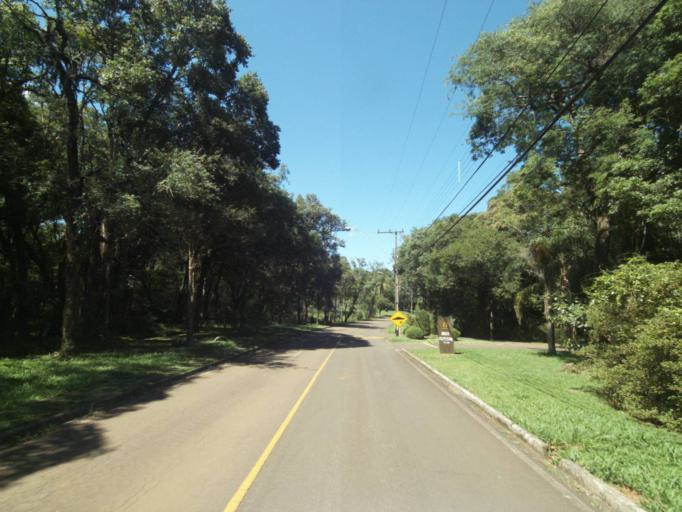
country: BR
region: Parana
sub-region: Chopinzinho
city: Chopinzinho
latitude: -25.7963
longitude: -52.0953
